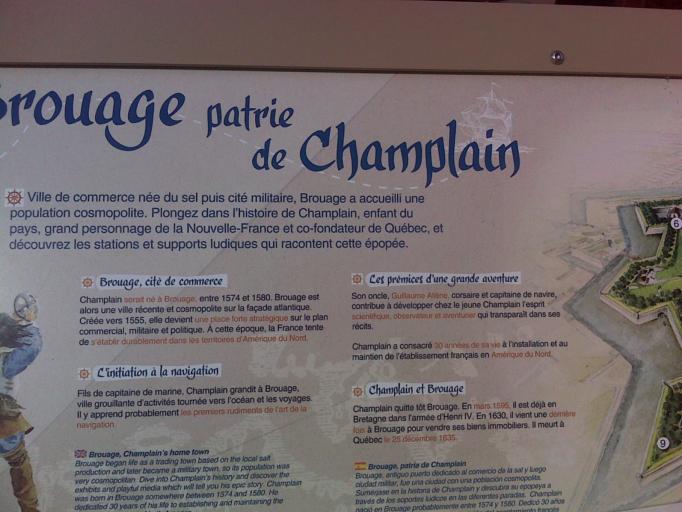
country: FR
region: Poitou-Charentes
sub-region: Departement de la Charente-Maritime
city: Marennes
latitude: 45.8664
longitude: -1.0705
